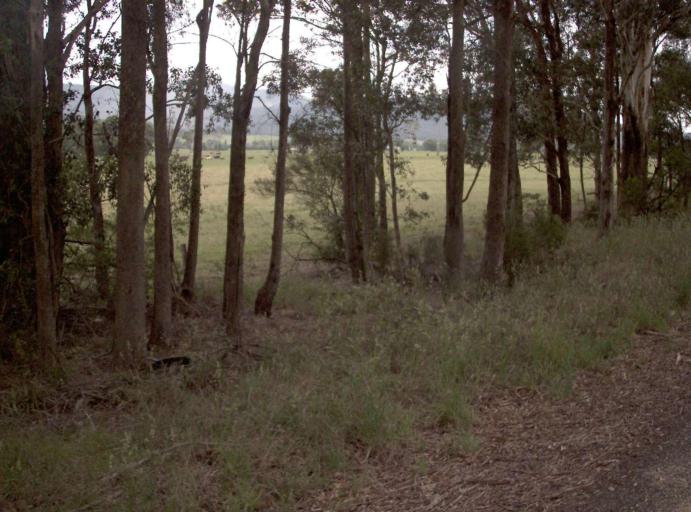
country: AU
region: New South Wales
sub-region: Bombala
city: Bombala
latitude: -37.5101
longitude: 149.1727
